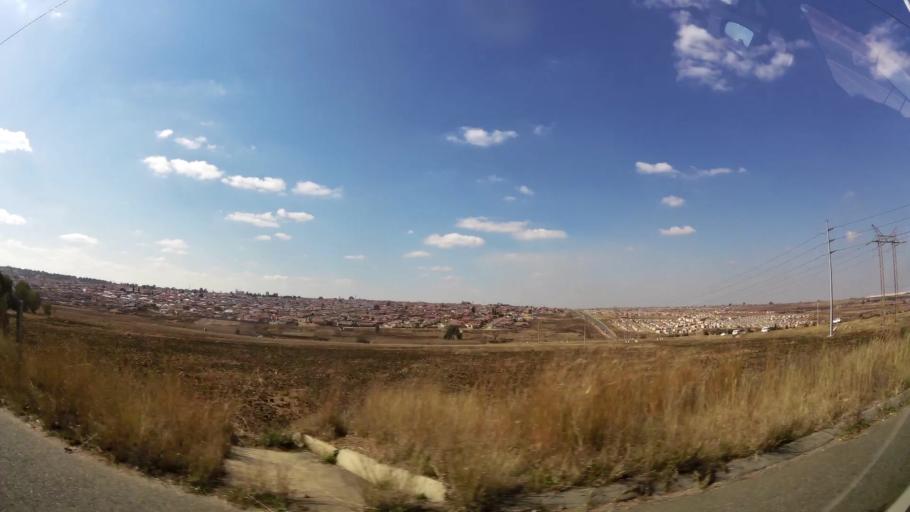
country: ZA
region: Gauteng
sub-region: West Rand District Municipality
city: Randfontein
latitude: -26.1625
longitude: 27.7615
